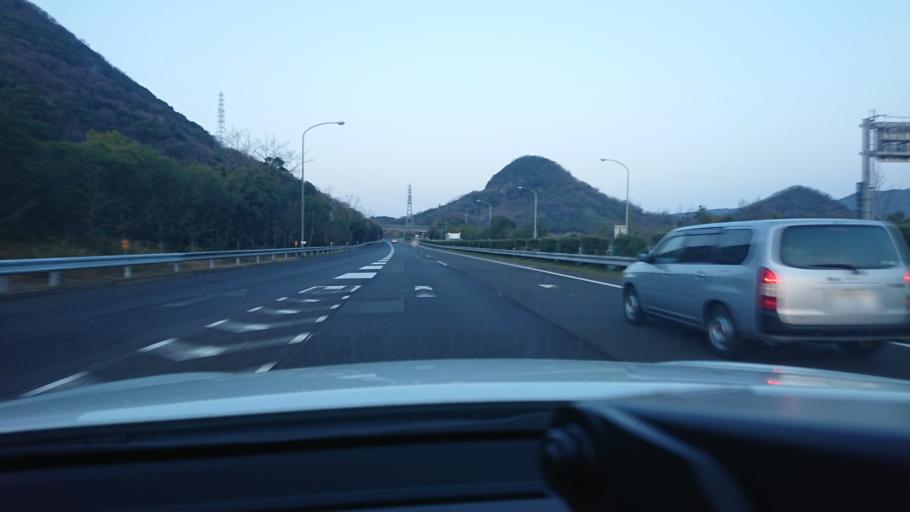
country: JP
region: Kagawa
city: Takamatsu-shi
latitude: 34.2953
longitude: 133.9852
